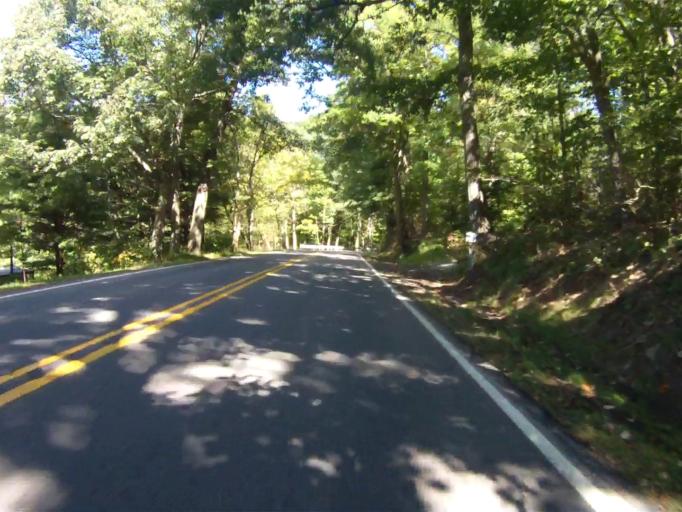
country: US
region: Pennsylvania
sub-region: Centre County
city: Park Forest Village
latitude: 40.9292
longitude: -77.9187
